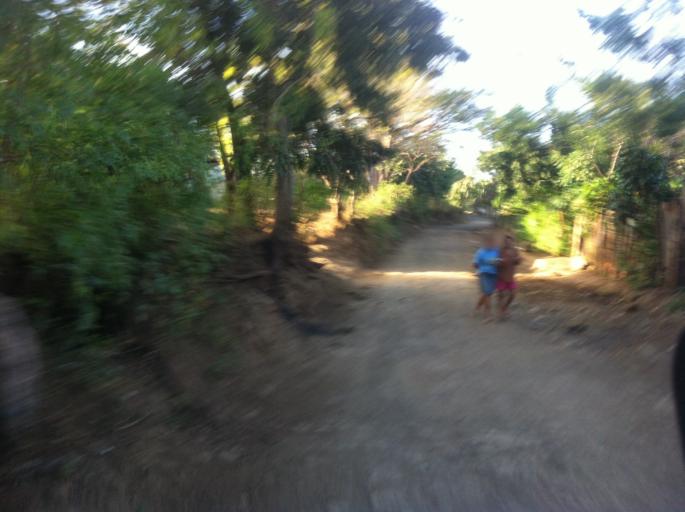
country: NI
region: Managua
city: Managua
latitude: 12.0854
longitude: -86.3115
